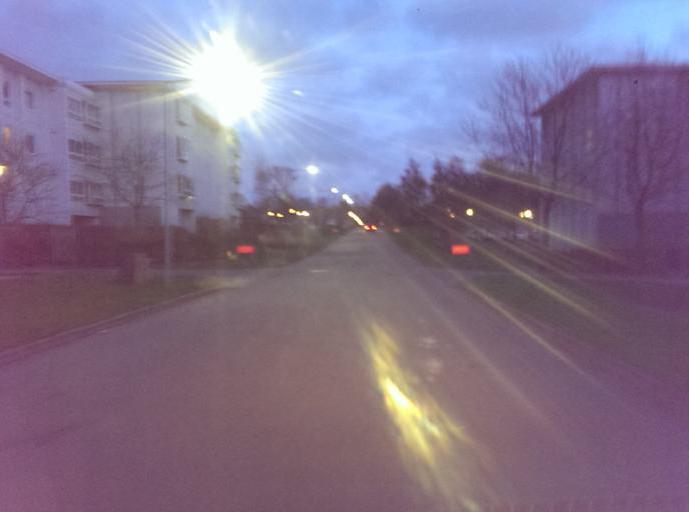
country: DK
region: South Denmark
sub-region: Esbjerg Kommune
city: Esbjerg
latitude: 55.4932
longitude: 8.4957
